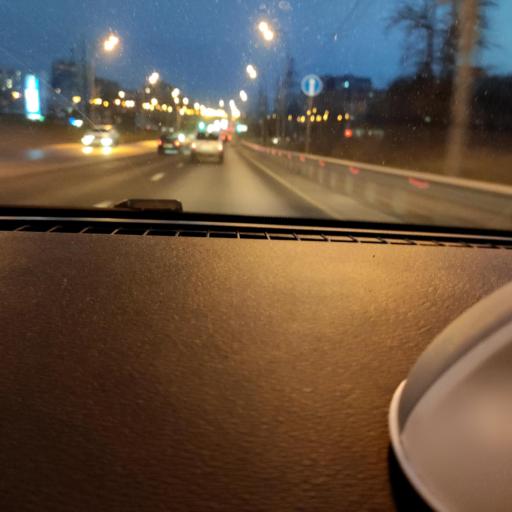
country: RU
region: Samara
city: Samara
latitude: 53.2719
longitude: 50.2242
